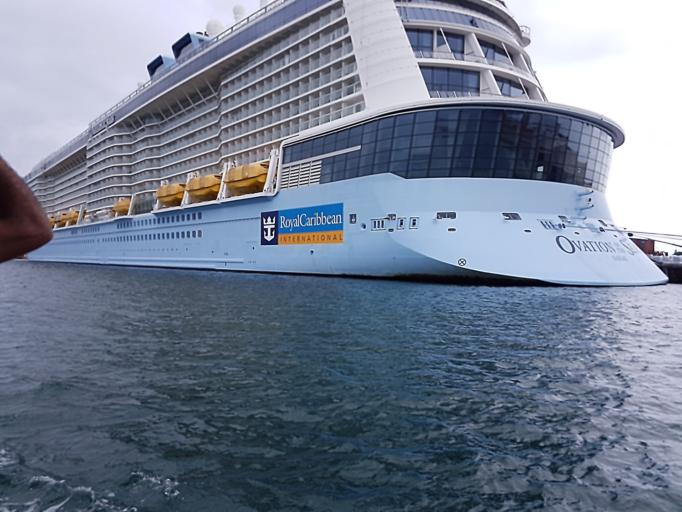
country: NZ
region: Bay of Plenty
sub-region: Tauranga City
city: Tauranga
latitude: -37.6457
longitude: 176.1812
